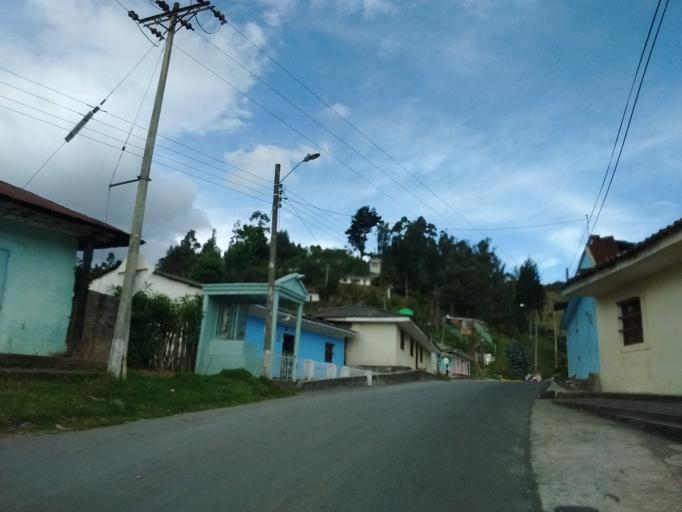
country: CO
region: Cauca
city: Totoro
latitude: 2.3819
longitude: -76.4522
